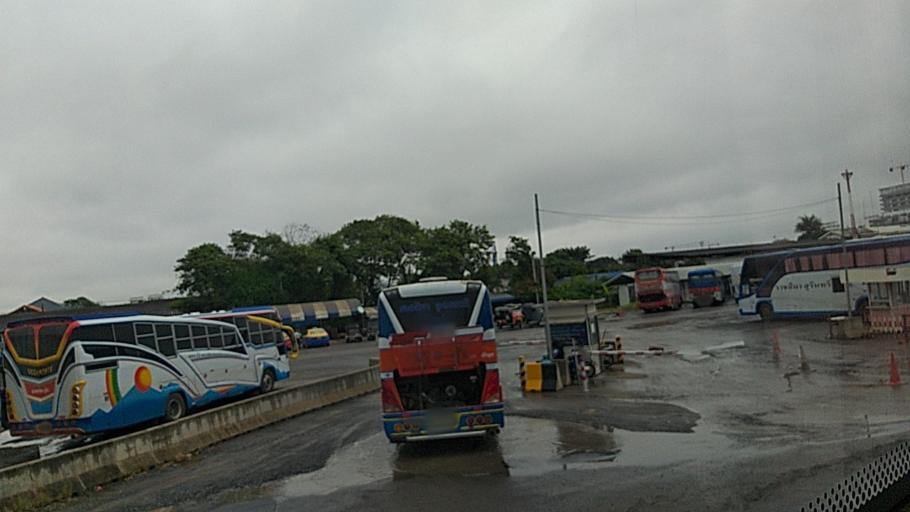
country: TH
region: Nakhon Ratchasima
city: Nakhon Ratchasima
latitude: 14.9911
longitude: 102.0943
